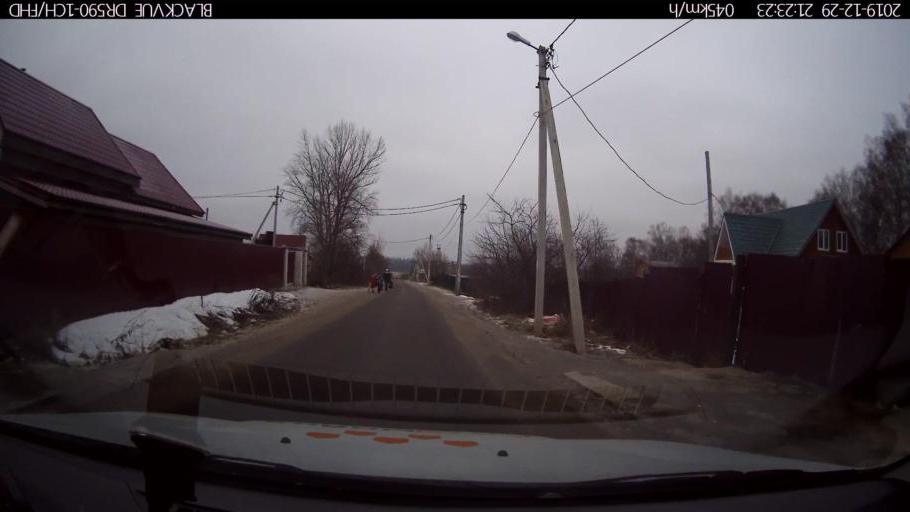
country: RU
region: Nizjnij Novgorod
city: Afonino
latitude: 56.2219
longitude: 44.0385
